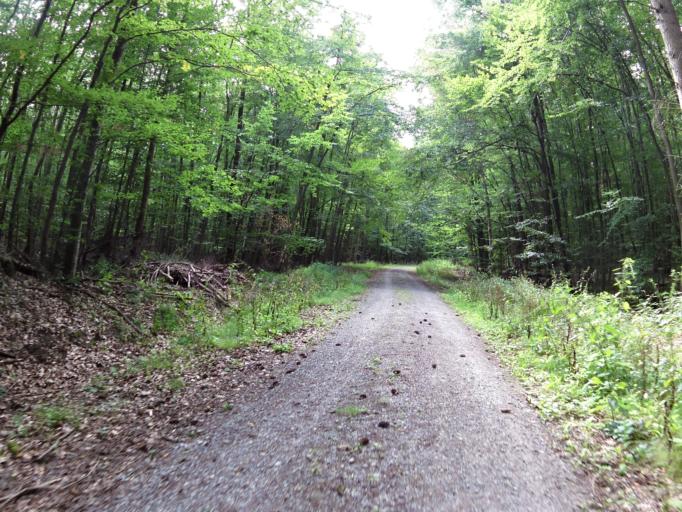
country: DE
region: Bavaria
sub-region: Regierungsbezirk Unterfranken
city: Kist
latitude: 49.7210
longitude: 9.8167
